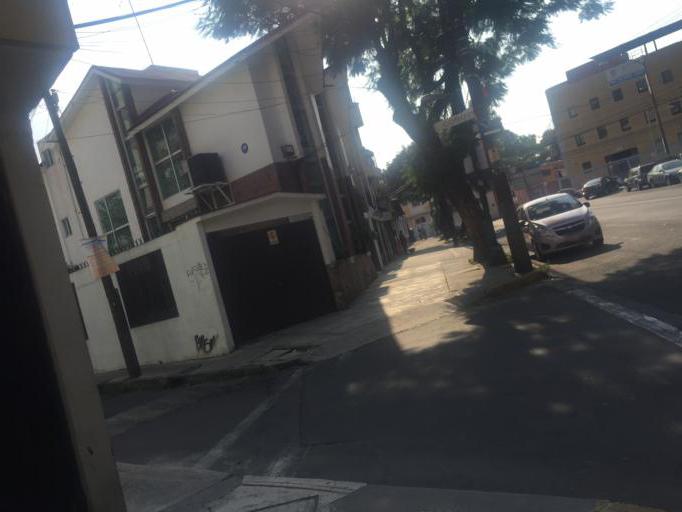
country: MX
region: Mexico City
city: Colonia del Valle
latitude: 19.3786
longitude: -99.1814
